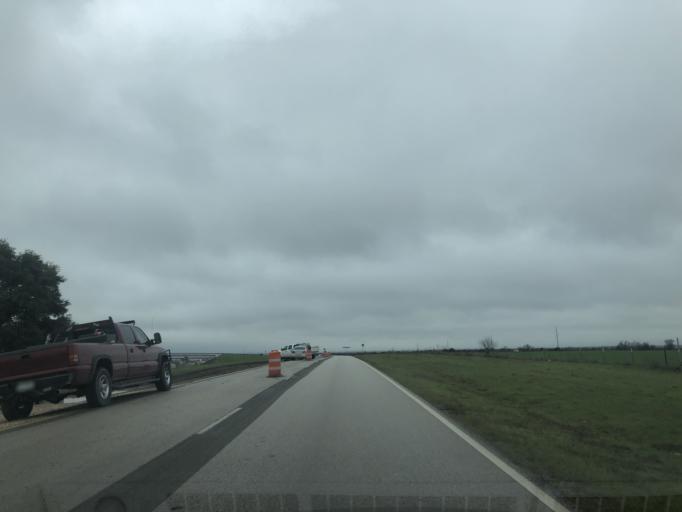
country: US
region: Texas
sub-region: Williamson County
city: Serenada
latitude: 30.7384
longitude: -97.6399
